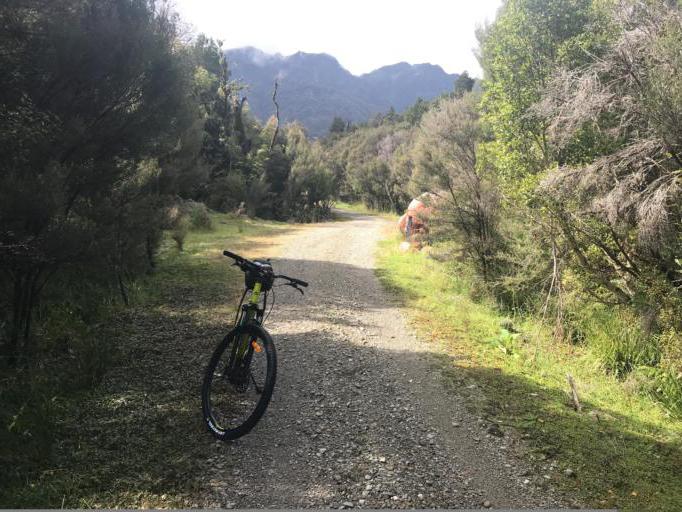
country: NZ
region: West Coast
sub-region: Westland District
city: Hokitika
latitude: -42.7868
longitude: 171.2706
